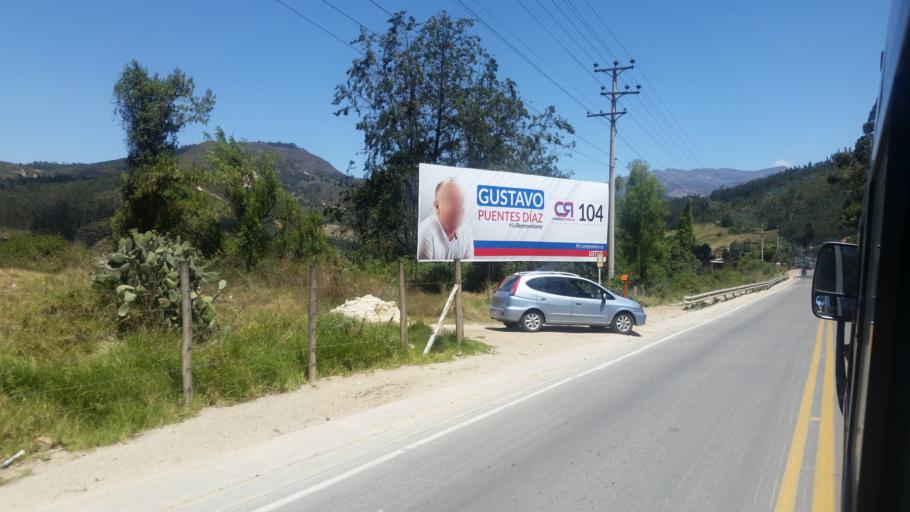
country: CO
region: Boyaca
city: Topaga
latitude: 5.7667
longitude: -72.8695
